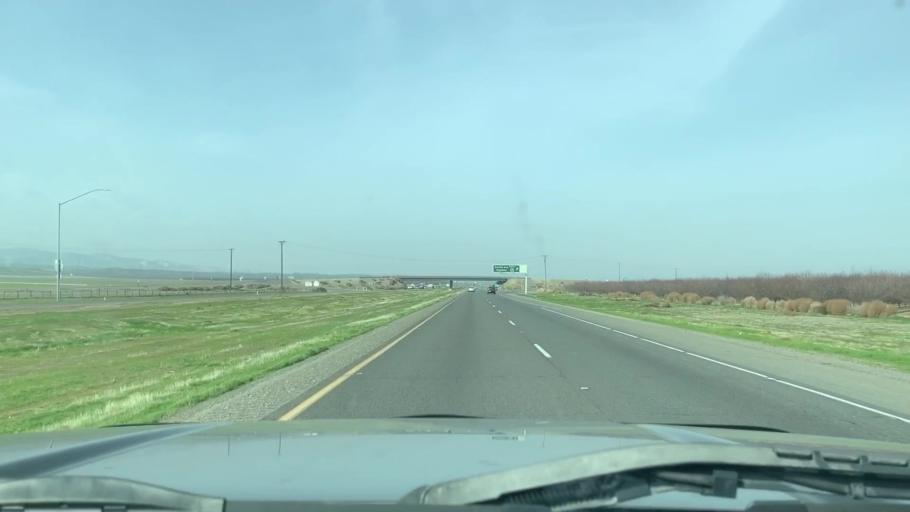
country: US
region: California
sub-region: Fresno County
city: San Joaquin
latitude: 36.4321
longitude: -120.3907
